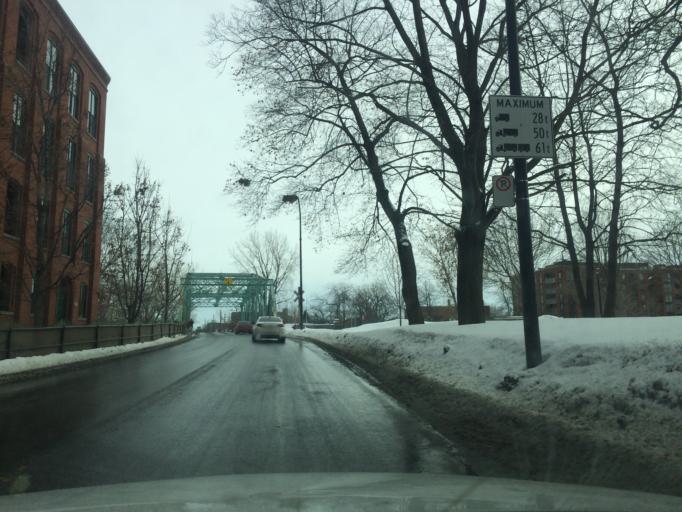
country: CA
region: Quebec
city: Westmount
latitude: 45.4809
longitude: -73.5735
